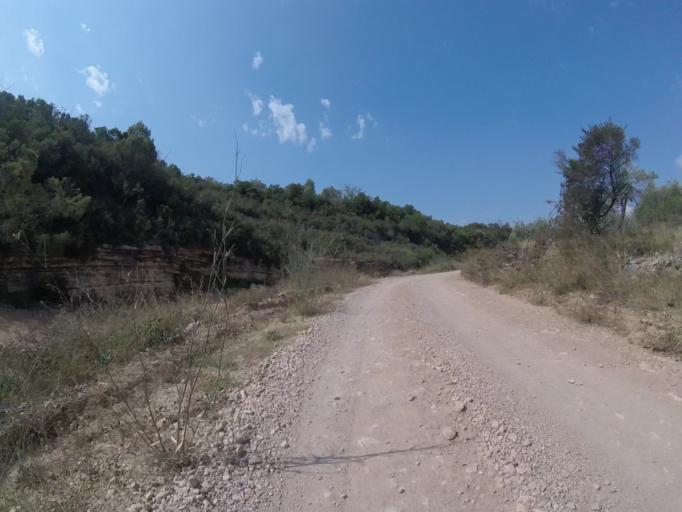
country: ES
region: Valencia
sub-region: Provincia de Castello
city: Cuevas de Vinroma
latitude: 40.3088
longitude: 0.1763
